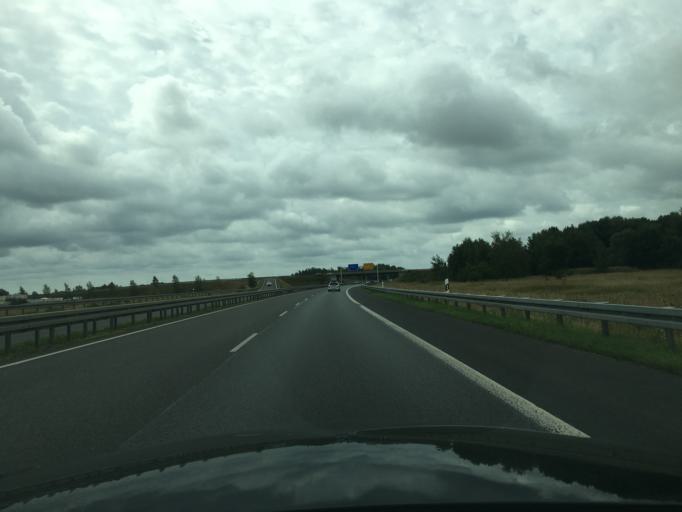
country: DE
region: Brandenburg
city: Leegebruch
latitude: 52.7235
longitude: 13.2172
